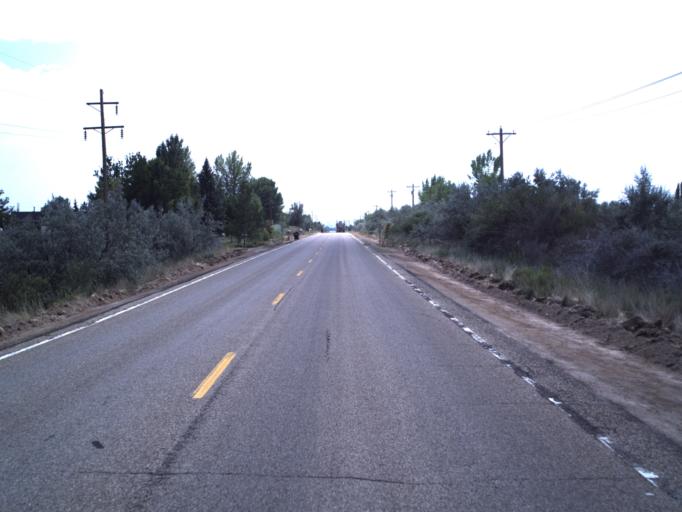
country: US
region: Utah
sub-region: Duchesne County
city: Roosevelt
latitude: 40.3790
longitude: -110.0298
